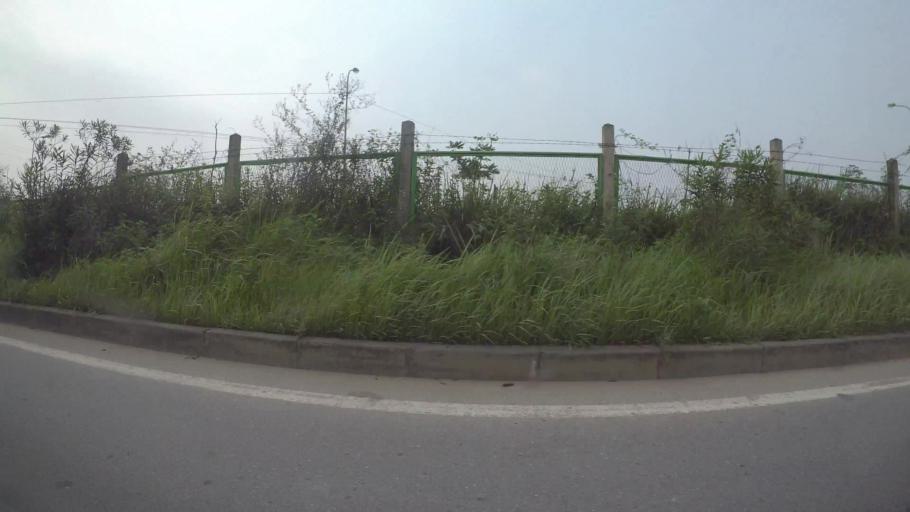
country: VN
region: Ha Noi
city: Quoc Oai
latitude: 21.0032
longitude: 105.6323
